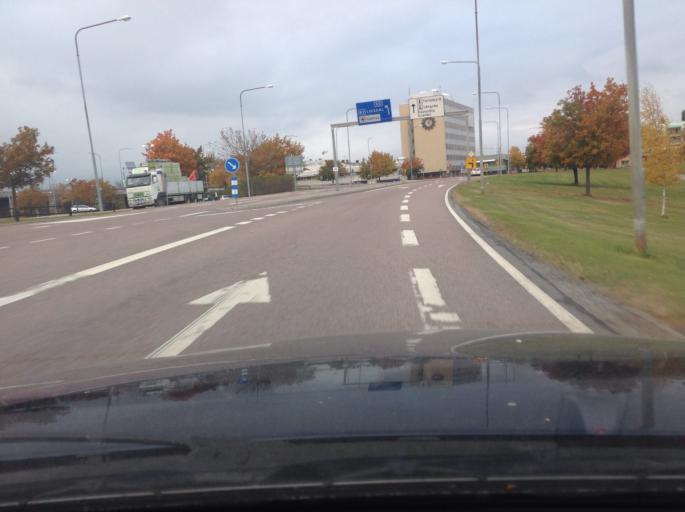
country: SE
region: Gaevleborg
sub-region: Bollnas Kommun
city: Bollnas
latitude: 61.3449
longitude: 16.3917
